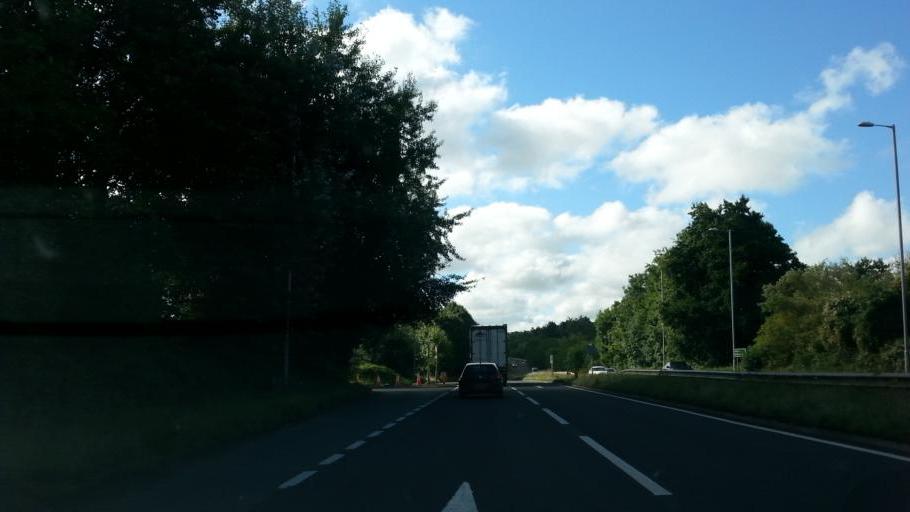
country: GB
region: England
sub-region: Northamptonshire
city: Northampton
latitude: 52.2621
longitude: -0.8414
